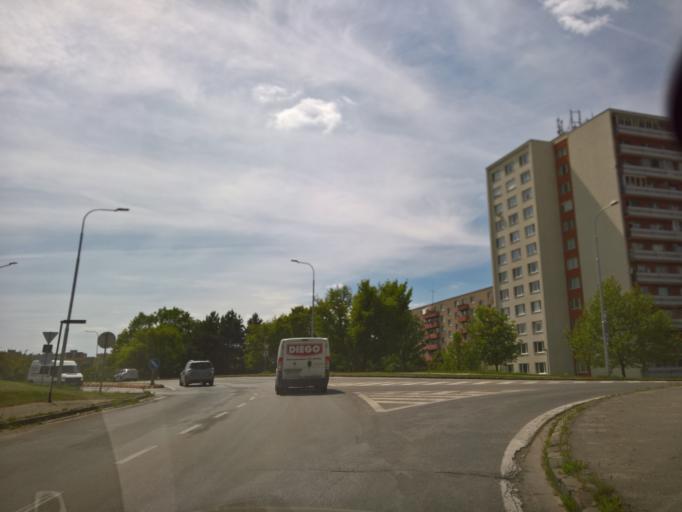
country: SK
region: Nitriansky
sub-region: Okres Nitra
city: Nitra
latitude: 48.3062
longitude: 18.0685
